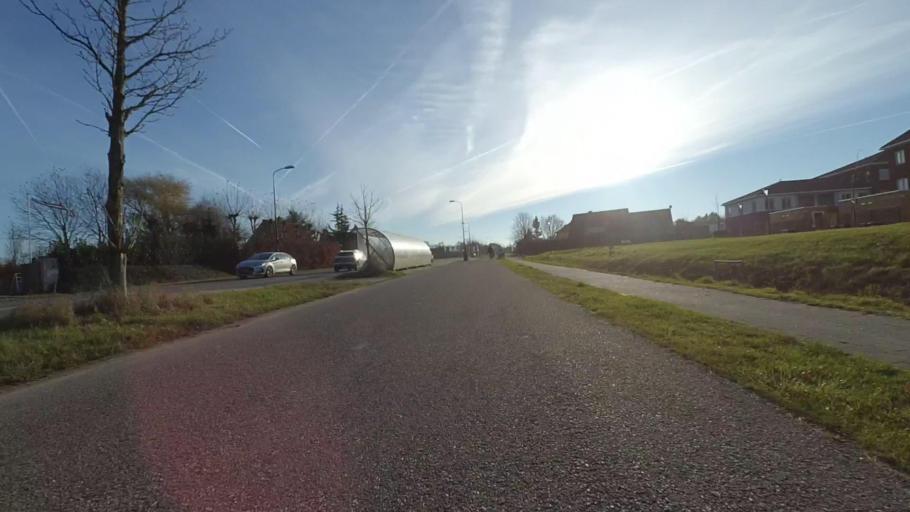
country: NL
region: Utrecht
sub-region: Gemeente Wijk bij Duurstede
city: Wijk bij Duurstede
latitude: 51.9849
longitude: 5.3367
